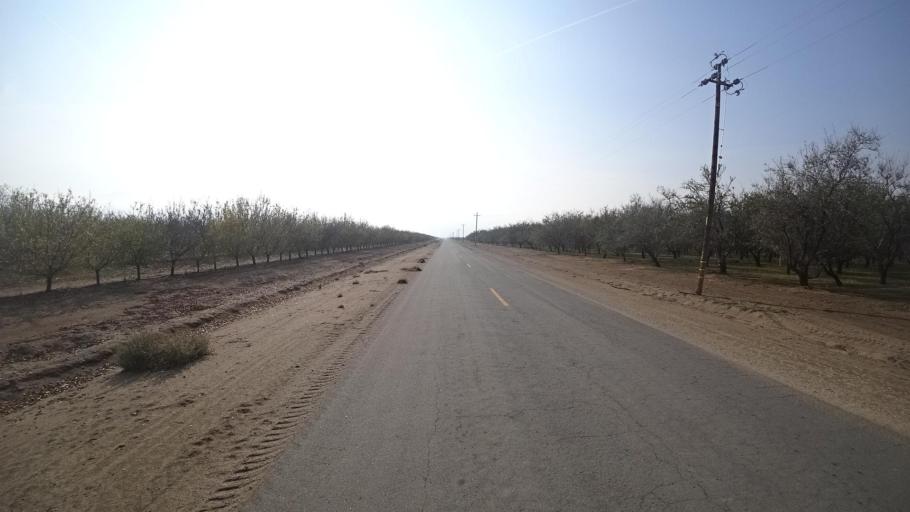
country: US
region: California
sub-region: Kern County
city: Lebec
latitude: 35.0044
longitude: -118.8466
